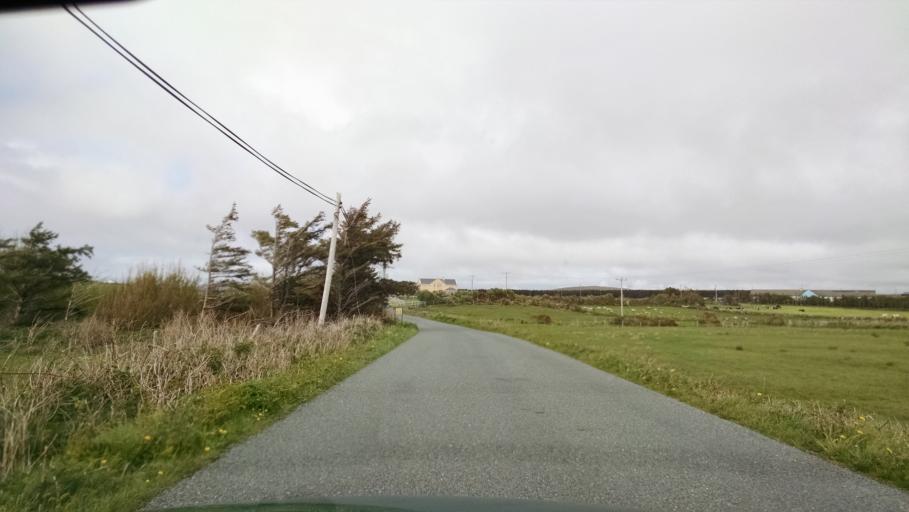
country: IE
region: Connaught
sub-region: County Galway
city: Clifden
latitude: 53.7156
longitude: -9.8796
